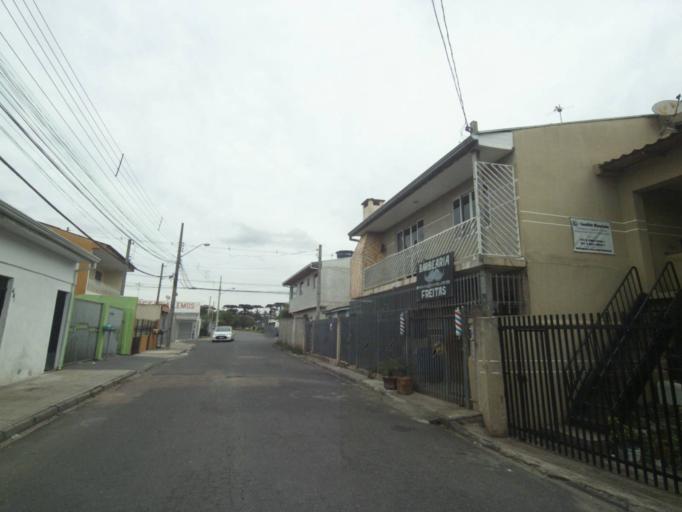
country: BR
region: Parana
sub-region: Curitiba
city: Curitiba
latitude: -25.5171
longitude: -49.3305
